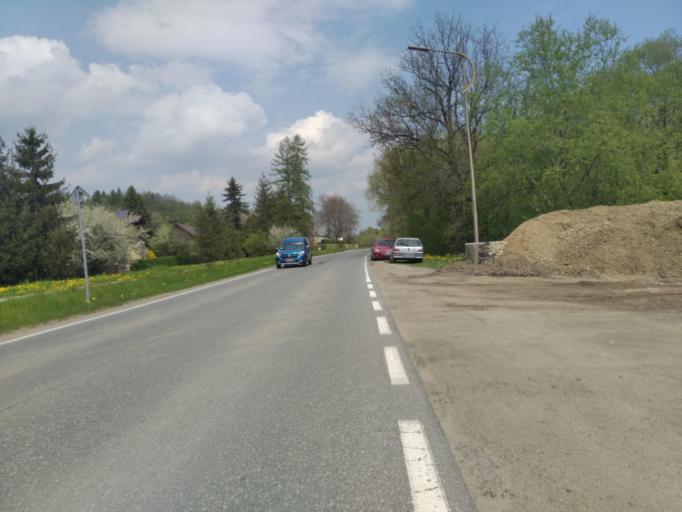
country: PL
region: Subcarpathian Voivodeship
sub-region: Powiat krosnienski
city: Rymanow
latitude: 49.5669
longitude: 21.8634
